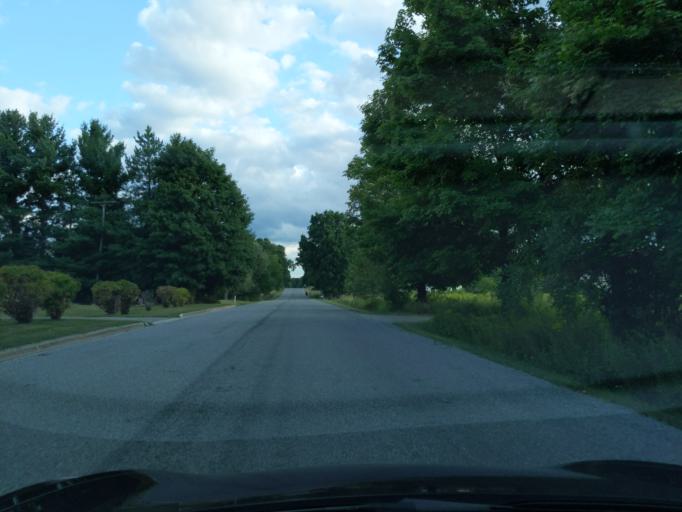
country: US
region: Michigan
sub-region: Ingham County
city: Holt
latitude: 42.6038
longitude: -84.5823
